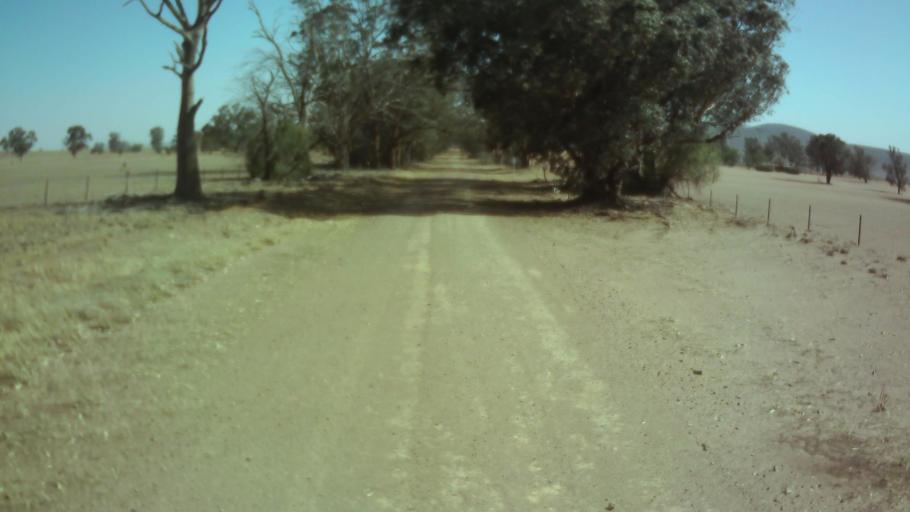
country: AU
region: New South Wales
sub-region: Weddin
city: Grenfell
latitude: -33.8425
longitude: 148.0178
